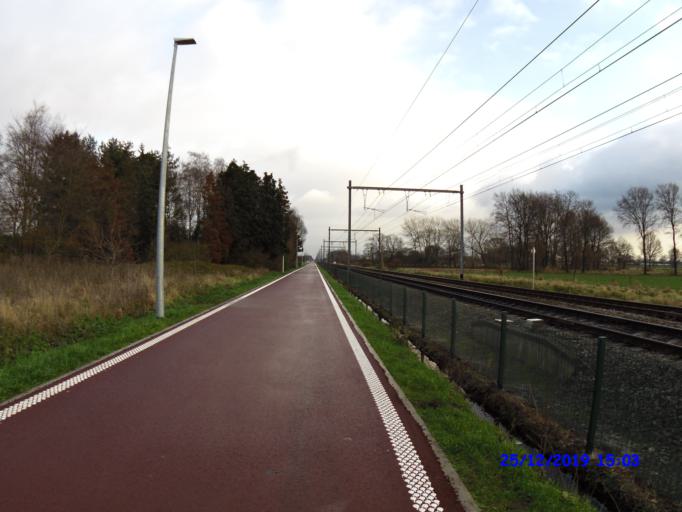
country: BE
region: Flanders
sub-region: Provincie Antwerpen
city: Geel
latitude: 51.1720
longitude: 4.9260
